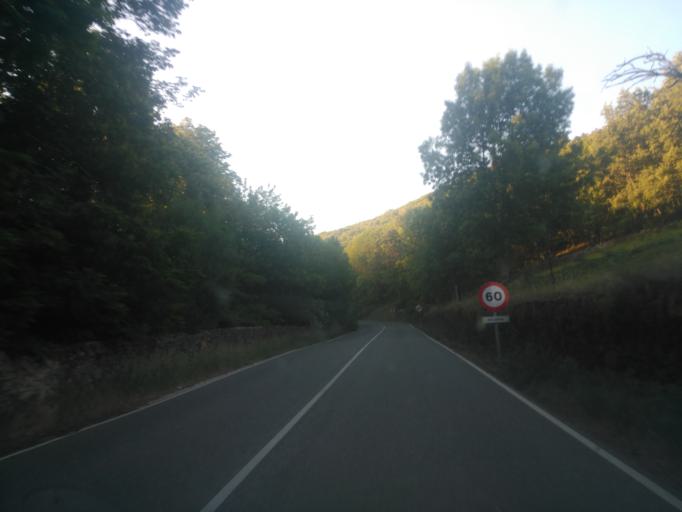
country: ES
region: Castille and Leon
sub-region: Provincia de Salamanca
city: Bejar
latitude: 40.3833
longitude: -5.7554
